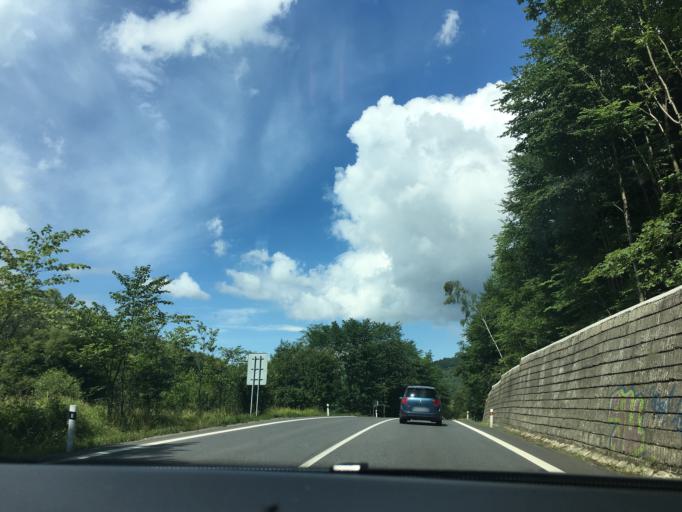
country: SK
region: Presovsky
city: Svidnik
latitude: 49.3678
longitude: 21.6906
